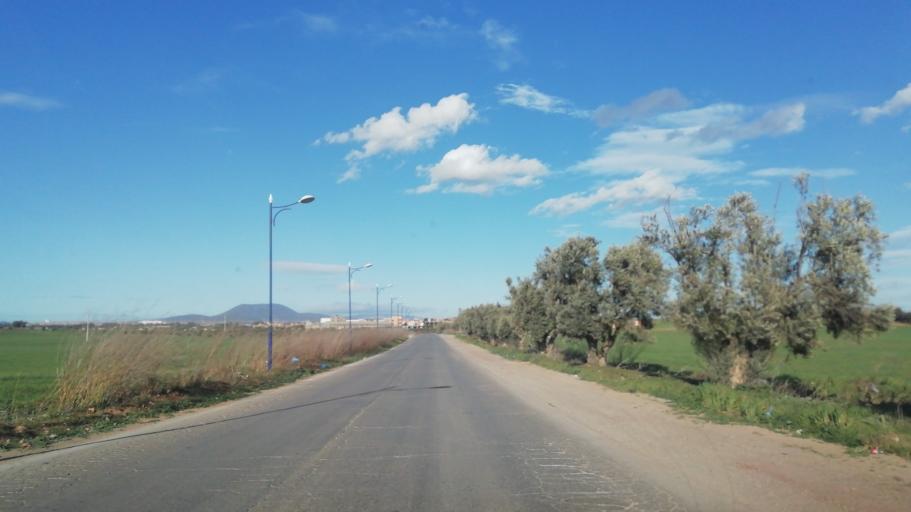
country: DZ
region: Oran
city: Sidi ech Chahmi
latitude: 35.6494
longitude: -0.5314
